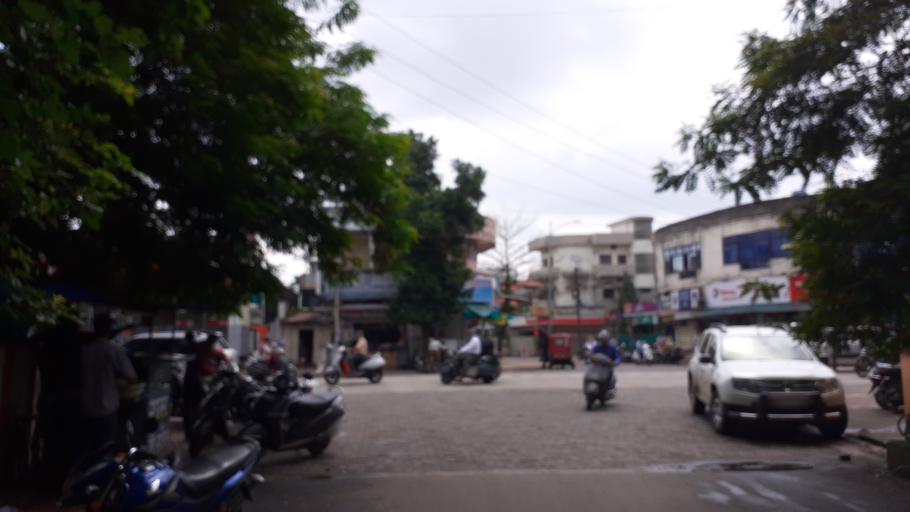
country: IN
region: Maharashtra
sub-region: Nagpur Division
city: Nagpur
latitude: 21.1293
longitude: 79.1138
